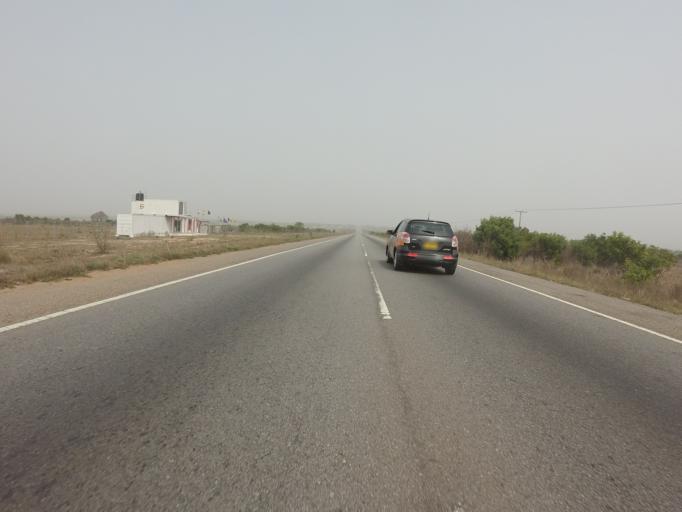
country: GH
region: Greater Accra
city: Tema
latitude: 5.8596
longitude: 0.2751
